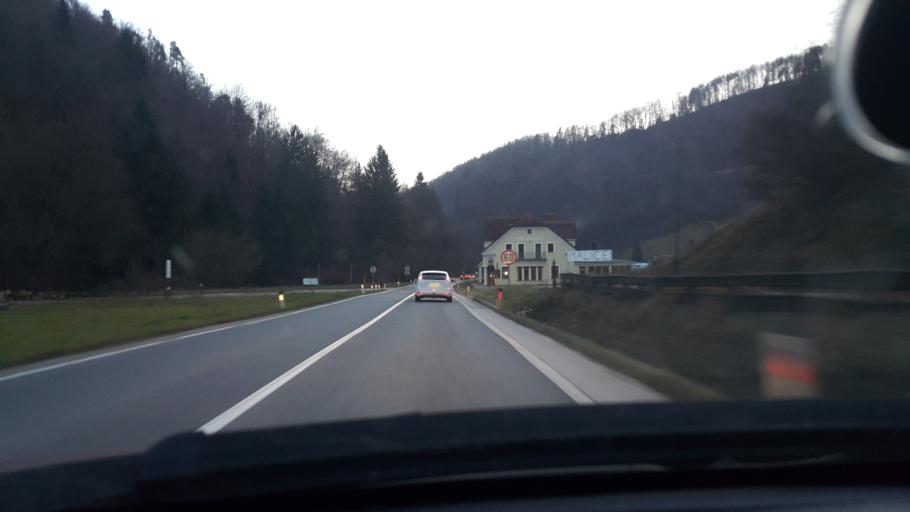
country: SI
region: Zalec
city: Gotovlje
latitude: 46.3006
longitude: 15.1718
